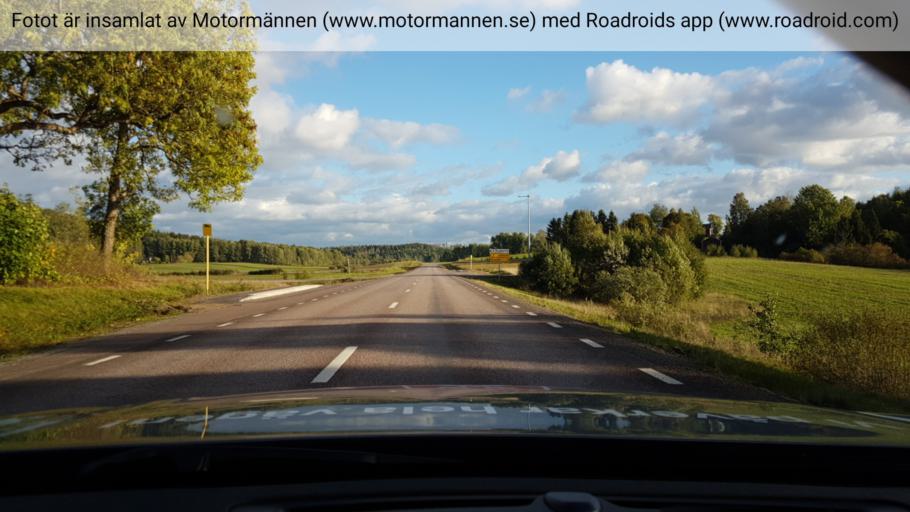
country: SE
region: Vaermland
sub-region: Karlstads Kommun
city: Molkom
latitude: 59.6340
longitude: 13.7226
